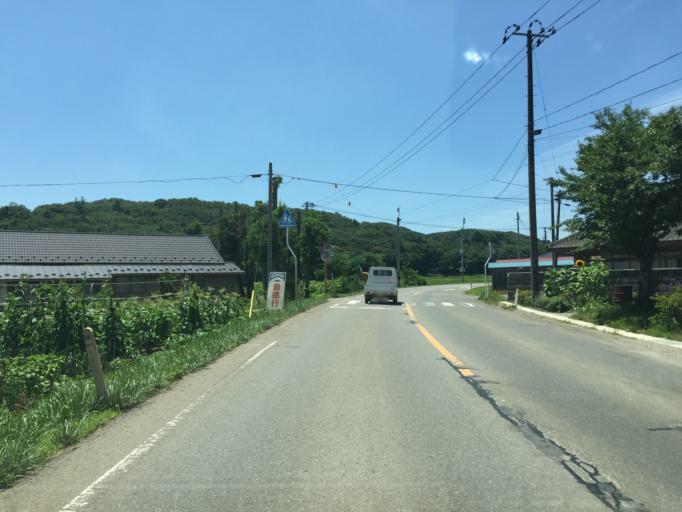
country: JP
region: Miyagi
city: Marumori
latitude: 37.7652
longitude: 140.7401
